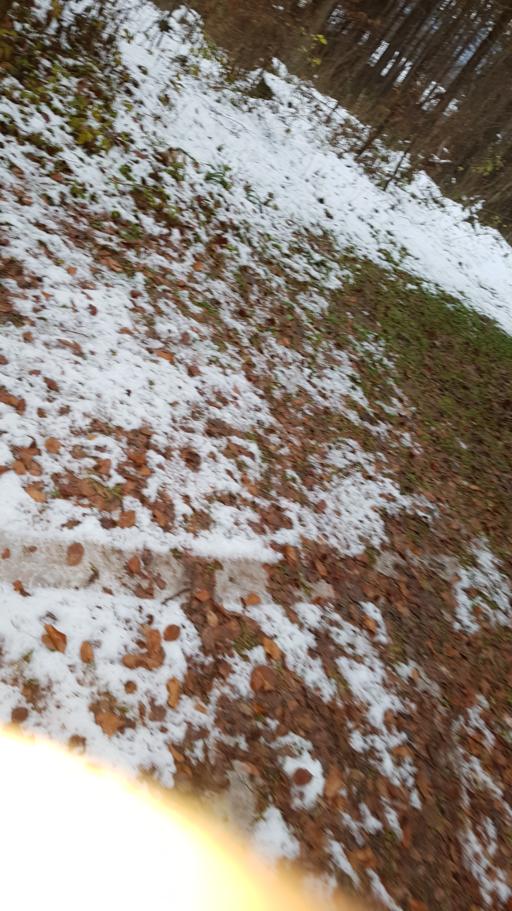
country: AT
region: Salzburg
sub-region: Politischer Bezirk Salzburg-Umgebung
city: Grodig
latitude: 47.7245
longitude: 13.0367
